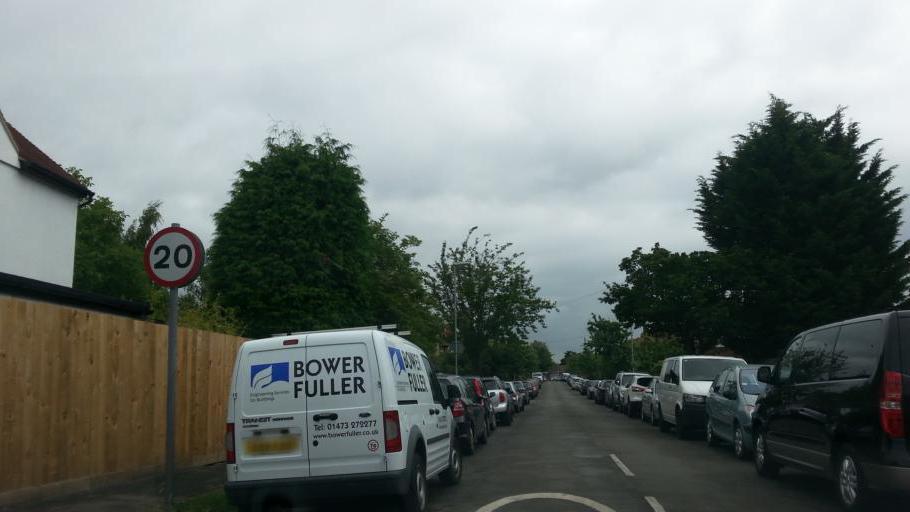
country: GB
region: England
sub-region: Cambridgeshire
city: Cambridge
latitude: 52.2176
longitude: 0.1251
